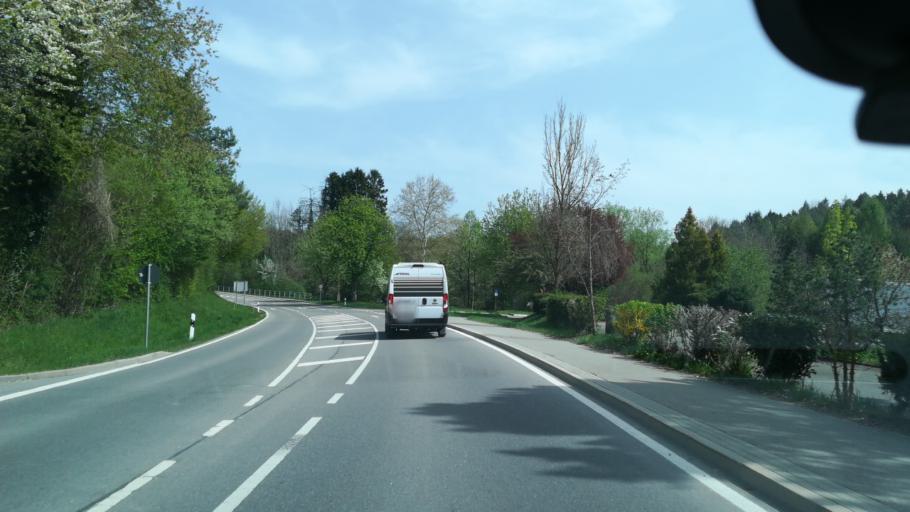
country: DE
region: Baden-Wuerttemberg
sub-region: Freiburg Region
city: Bodman-Ludwigshafen
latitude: 47.7723
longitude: 9.0209
